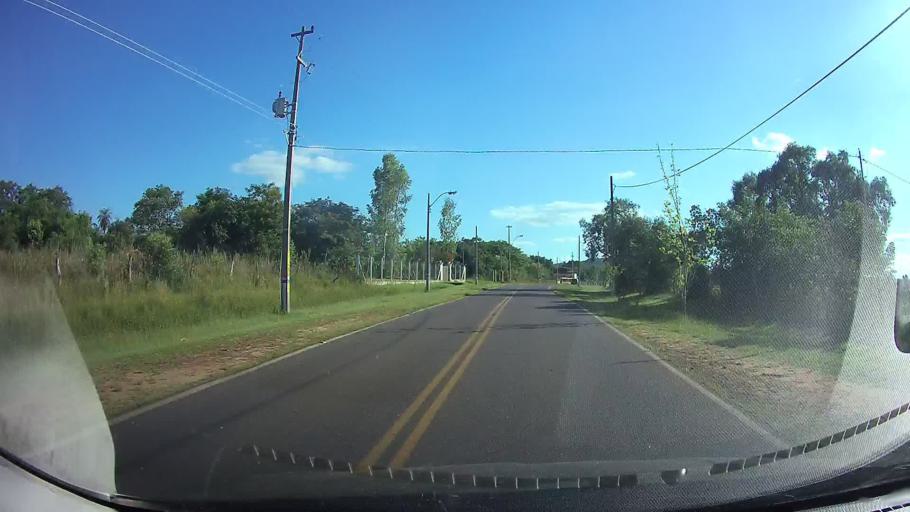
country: PY
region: Cordillera
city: Atyra
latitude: -25.3058
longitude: -57.1872
